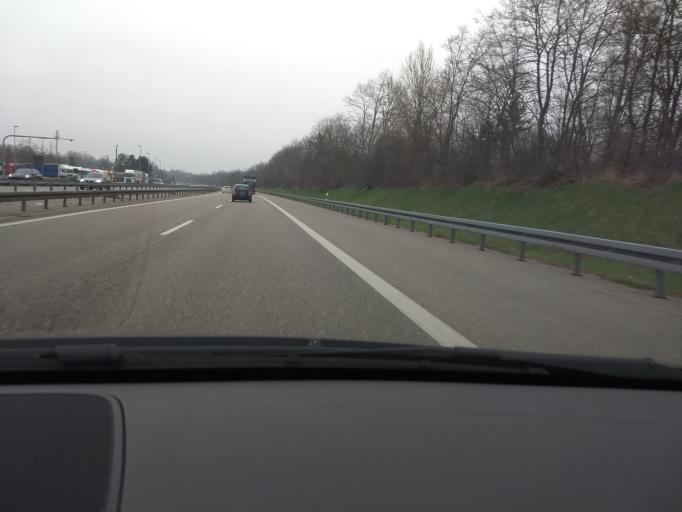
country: DE
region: Baden-Wuerttemberg
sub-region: Freiburg Region
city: Bad Bellingen
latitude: 47.7351
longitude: 7.5521
